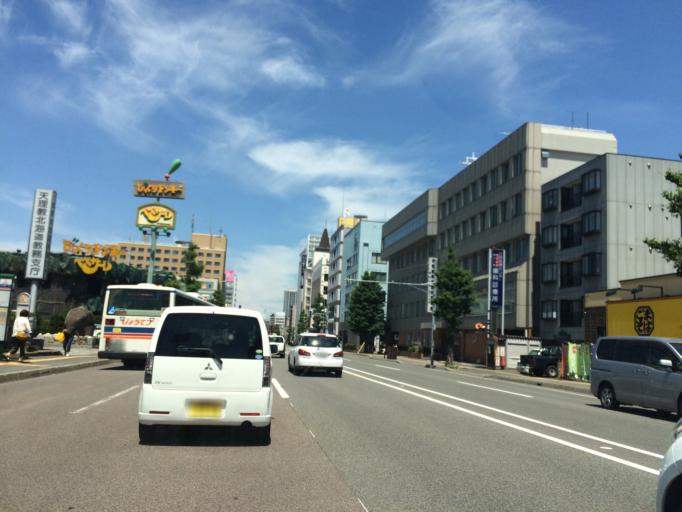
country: JP
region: Hokkaido
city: Sapporo
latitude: 43.0495
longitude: 141.3425
